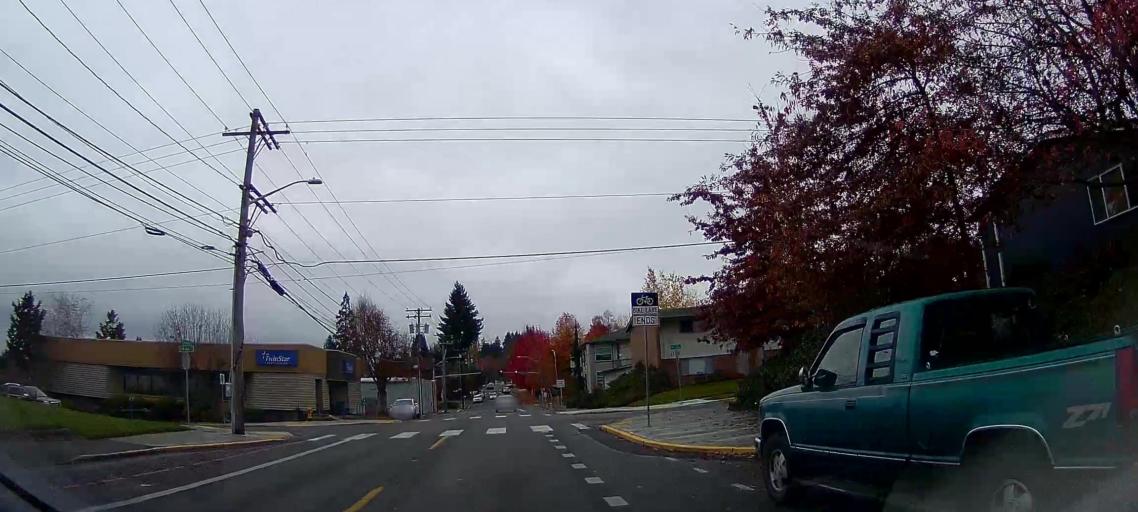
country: US
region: Washington
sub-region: Thurston County
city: Olympia
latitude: 47.0447
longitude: -122.8883
